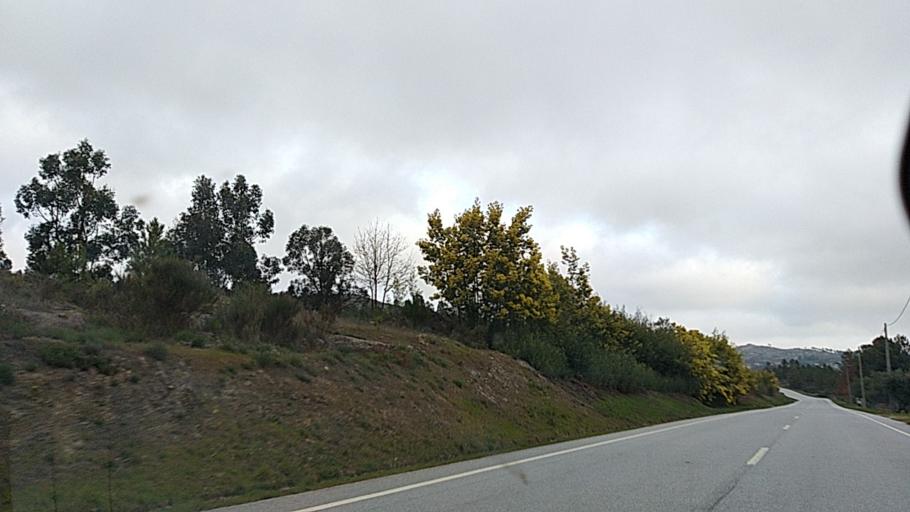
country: PT
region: Guarda
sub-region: Fornos de Algodres
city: Fornos de Algodres
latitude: 40.6414
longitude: -7.4933
